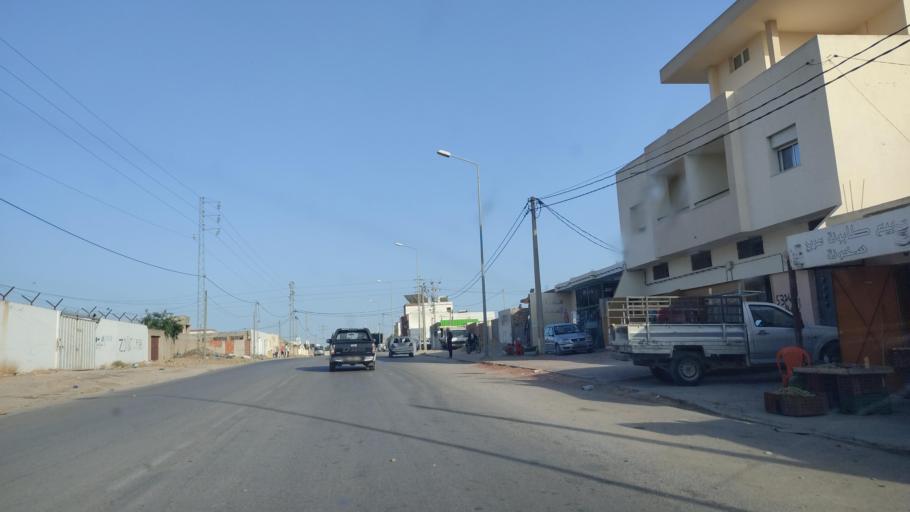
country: TN
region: Safaqis
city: Sfax
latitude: 34.7943
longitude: 10.6829
